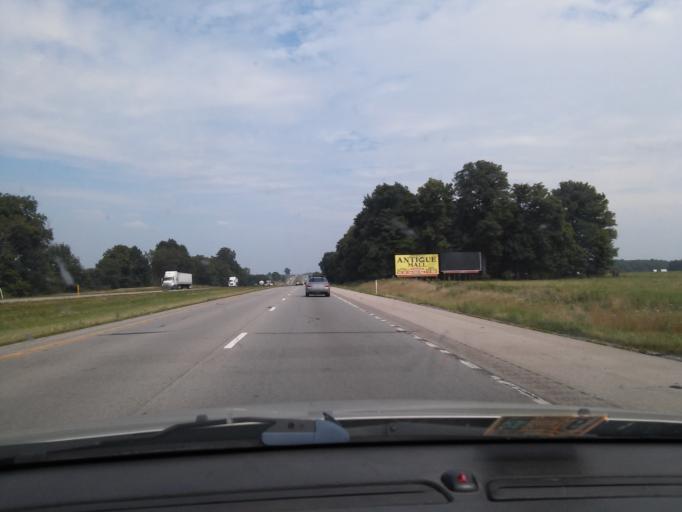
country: US
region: Indiana
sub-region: Wayne County
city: Cambridge City
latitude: 39.8533
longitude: -85.2095
